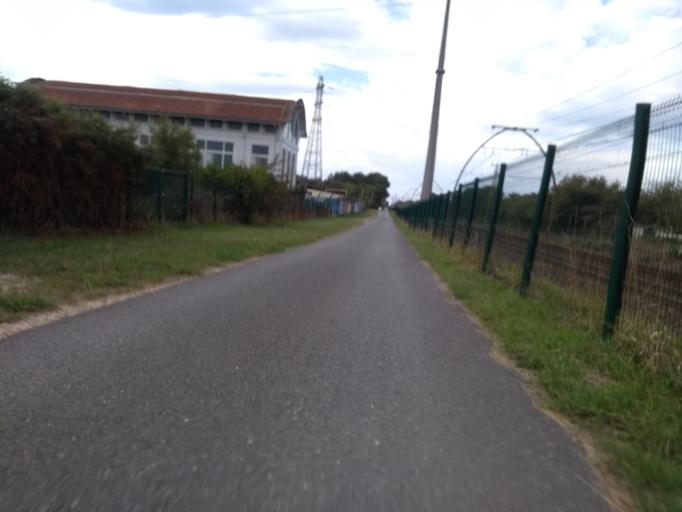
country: FR
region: Aquitaine
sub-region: Departement de la Gironde
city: Pessac
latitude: 44.7899
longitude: -0.6660
